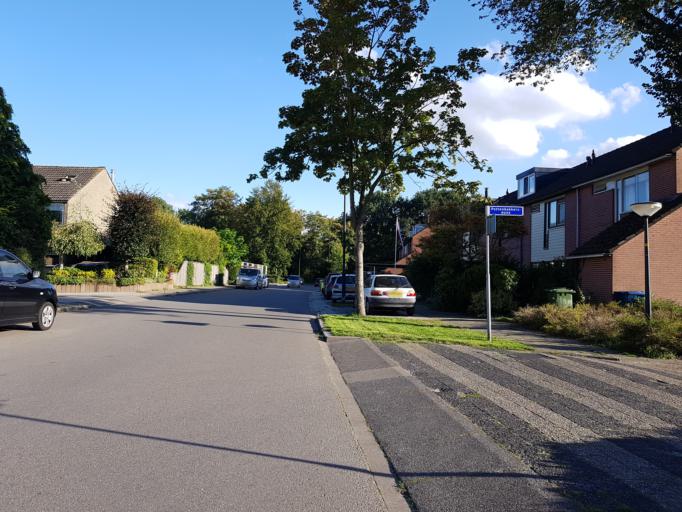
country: NL
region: Gelderland
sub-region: Gemeente Apeldoorn
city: Apeldoorn
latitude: 52.1963
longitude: 6.0156
